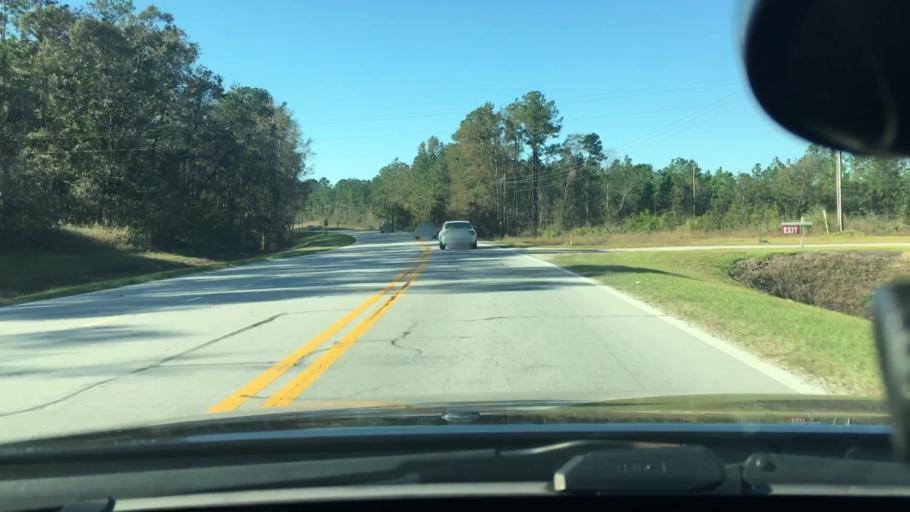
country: US
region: North Carolina
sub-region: Craven County
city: Vanceboro
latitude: 35.2175
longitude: -77.1213
